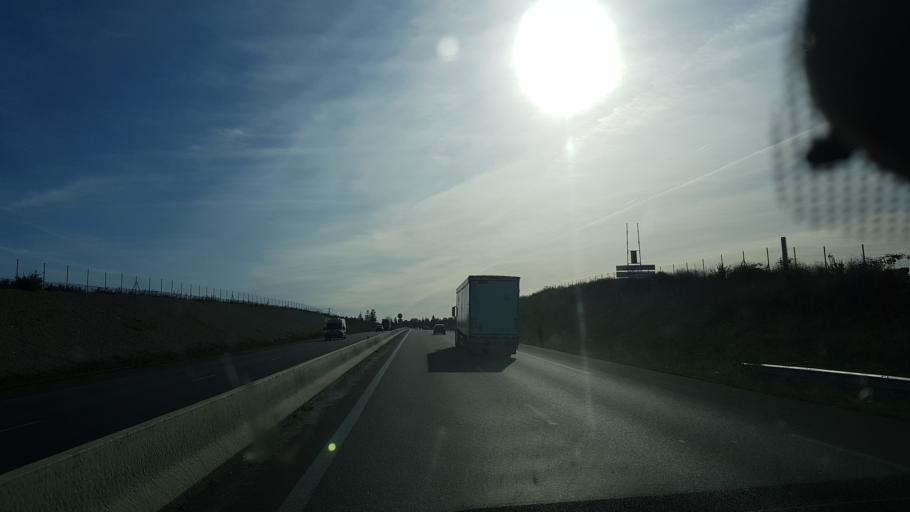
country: FR
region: Poitou-Charentes
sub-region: Departement de la Charente
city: Baignes-Sainte-Radegonde
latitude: 45.3542
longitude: -0.1977
